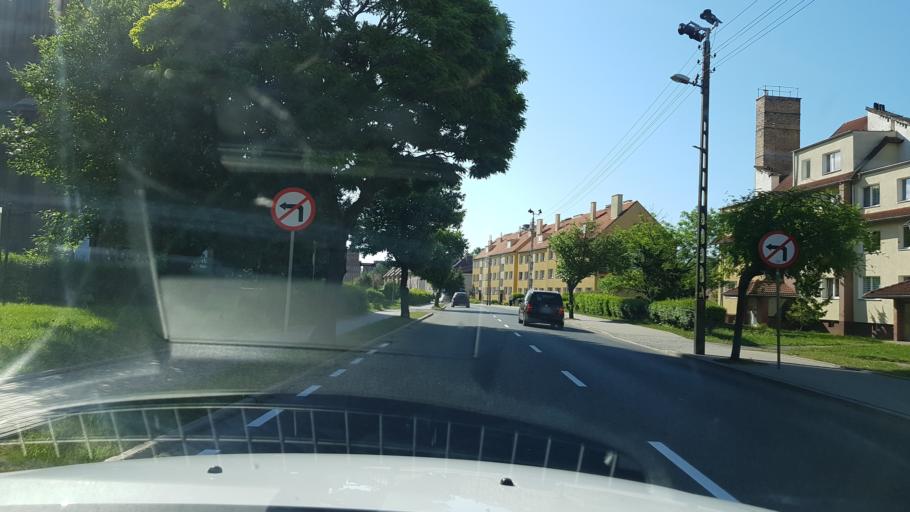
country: PL
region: West Pomeranian Voivodeship
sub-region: Powiat gryfinski
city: Chojna
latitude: 52.9630
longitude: 14.4285
